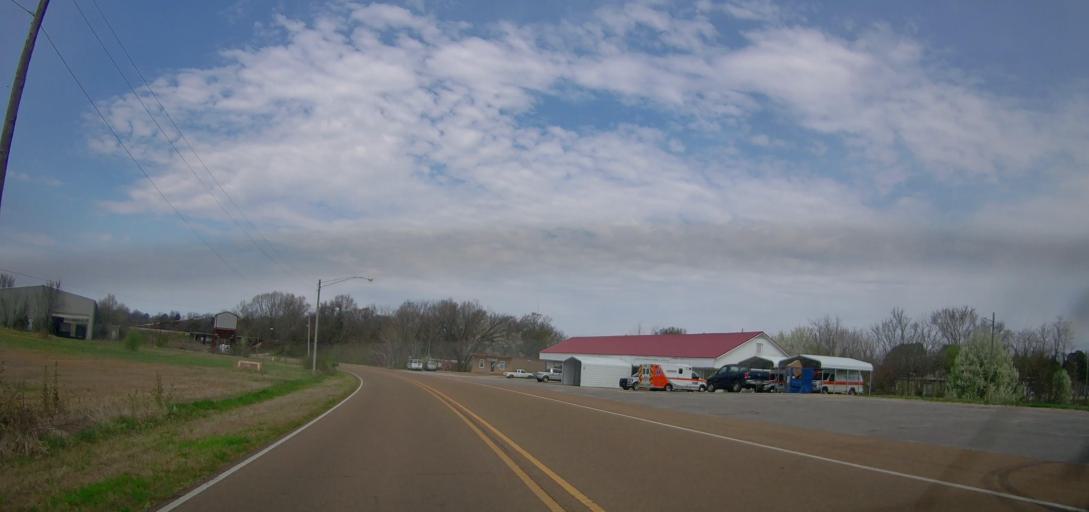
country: US
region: Mississippi
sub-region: Marshall County
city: Holly Springs
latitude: 34.7645
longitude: -89.4316
